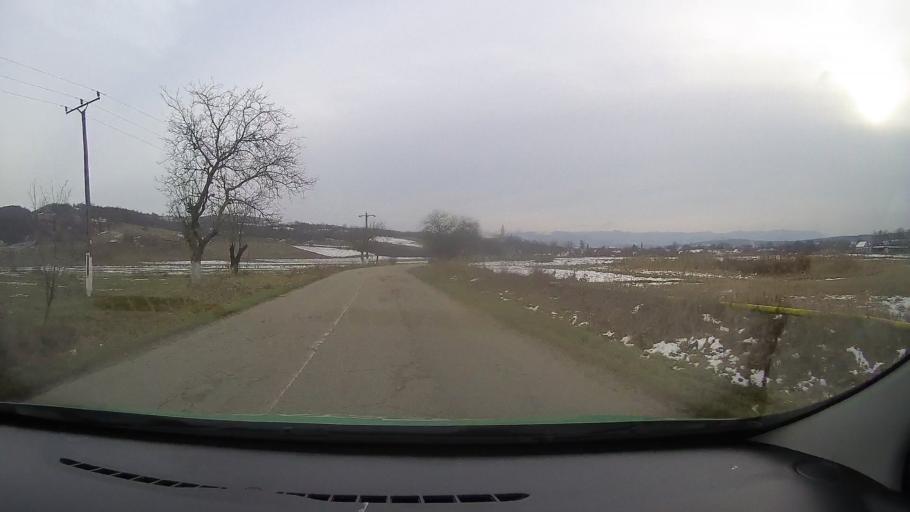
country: RO
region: Hunedoara
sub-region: Comuna Romos
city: Romos
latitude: 45.8552
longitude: 23.2725
